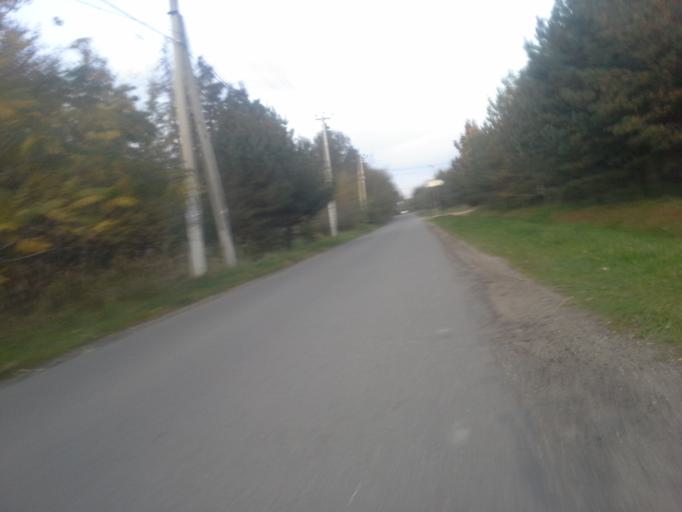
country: RU
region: Moskovskaya
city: Zhavoronki
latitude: 55.6462
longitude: 37.1417
